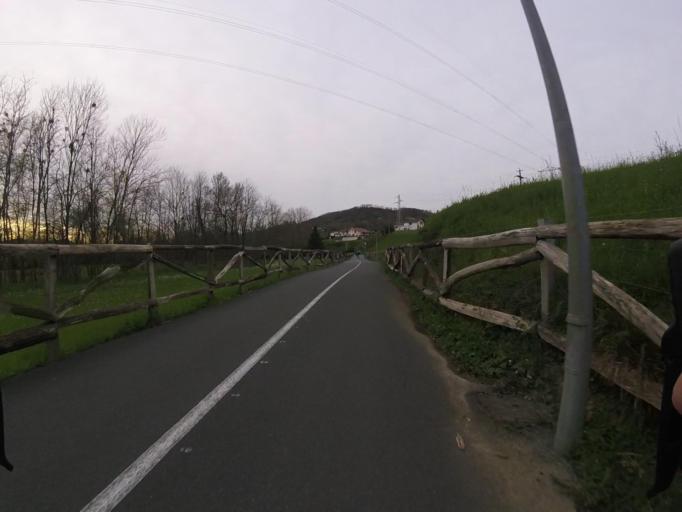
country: ES
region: Basque Country
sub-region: Provincia de Guipuzcoa
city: Lezo
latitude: 43.2933
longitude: -1.8494
